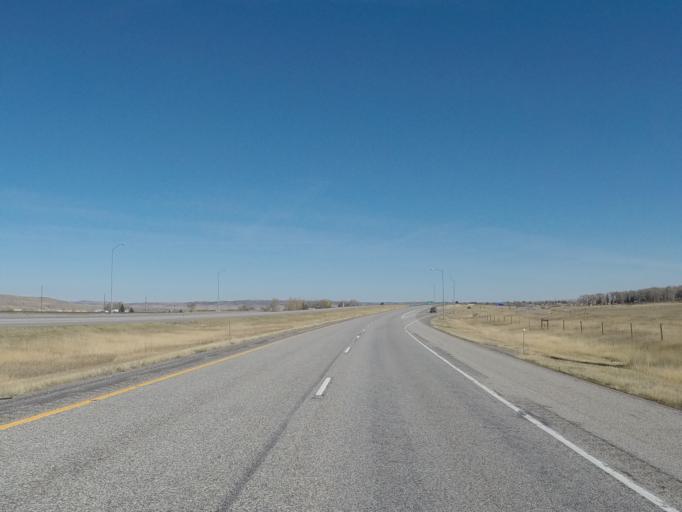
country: US
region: Montana
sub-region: Sweet Grass County
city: Big Timber
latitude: 45.8233
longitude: -109.9796
